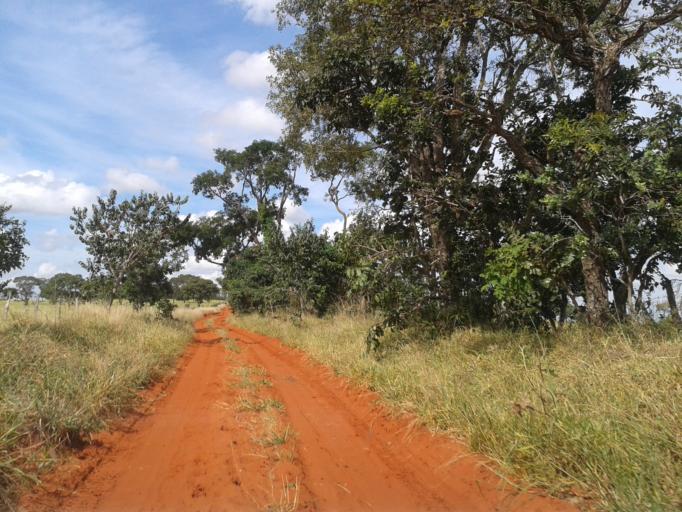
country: BR
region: Minas Gerais
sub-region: Campina Verde
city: Campina Verde
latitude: -19.4487
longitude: -49.6476
